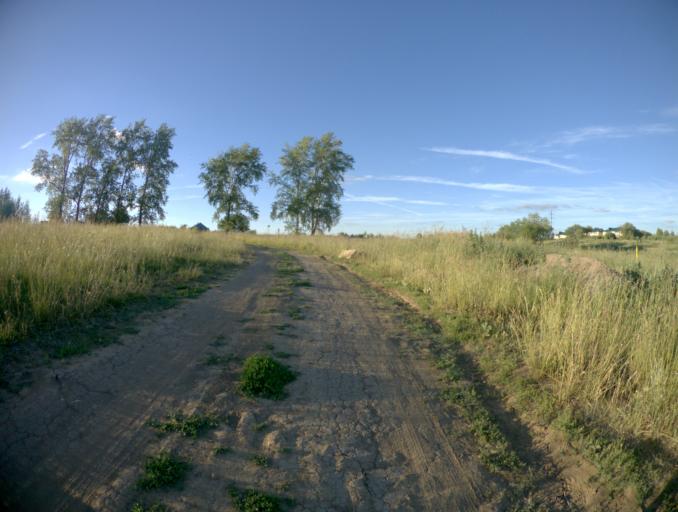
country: RU
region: Vladimir
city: Bogolyubovo
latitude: 56.1887
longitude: 40.5073
